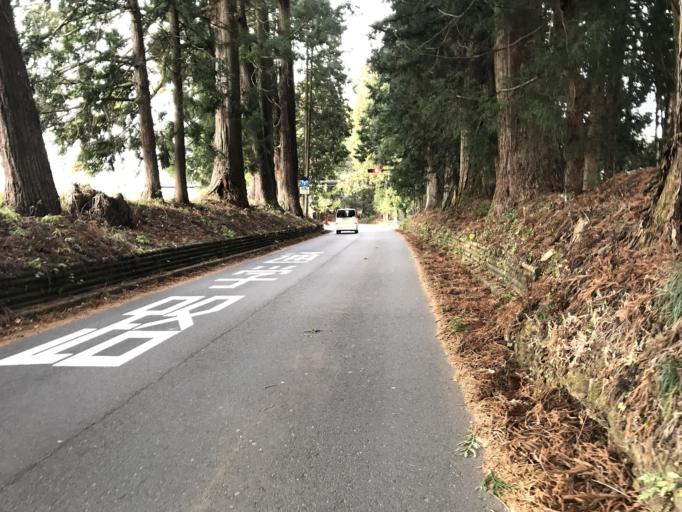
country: JP
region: Tochigi
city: Imaichi
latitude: 36.7204
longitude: 139.6916
